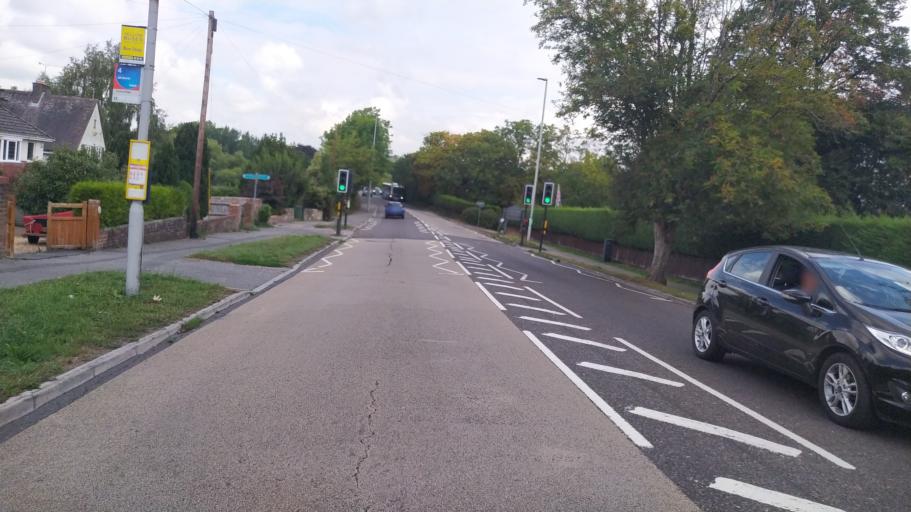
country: GB
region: England
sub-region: Dorset
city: Wimborne Minster
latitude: 50.7905
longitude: -1.9774
